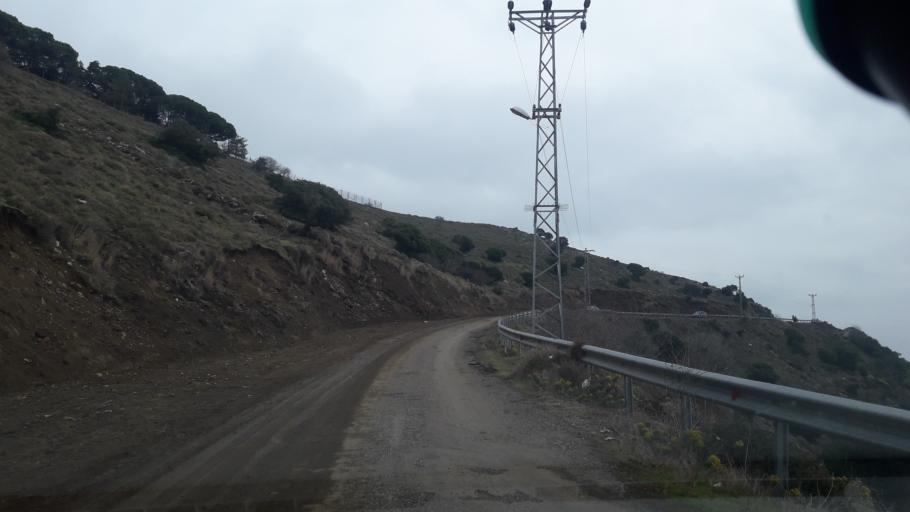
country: TR
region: Sinop
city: Sinop
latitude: 42.0174
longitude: 35.1996
